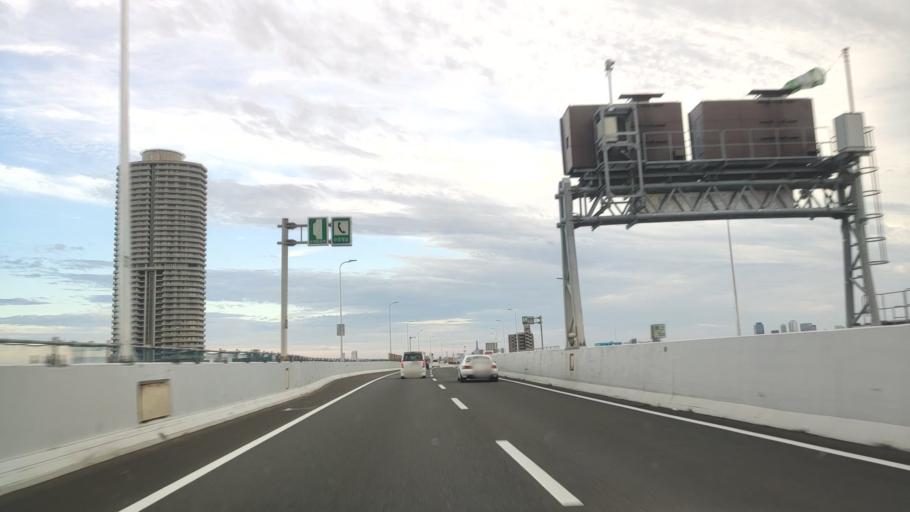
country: JP
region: Aichi
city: Nagoya-shi
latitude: 35.2204
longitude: 136.9105
